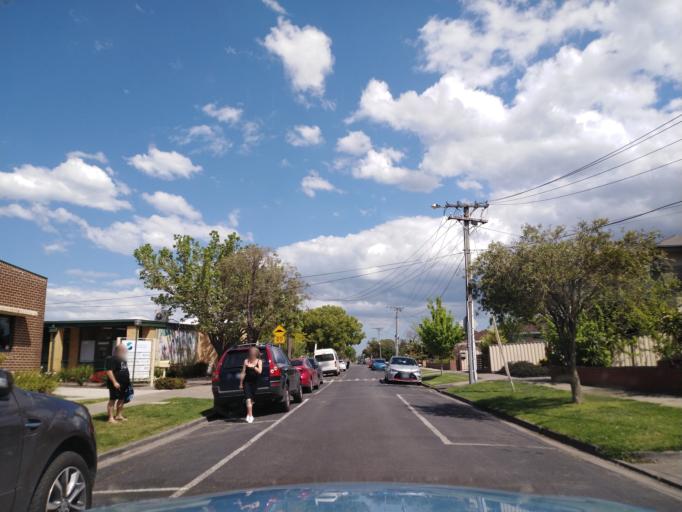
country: AU
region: Victoria
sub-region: Hobsons Bay
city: South Kingsville
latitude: -37.8287
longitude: 144.8700
